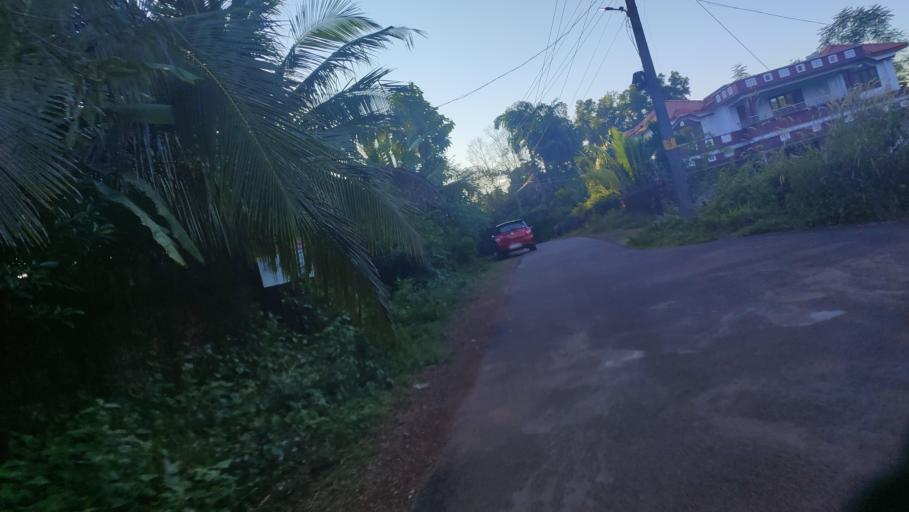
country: IN
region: Kerala
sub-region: Kasaragod District
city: Kannangad
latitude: 12.4021
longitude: 75.0594
